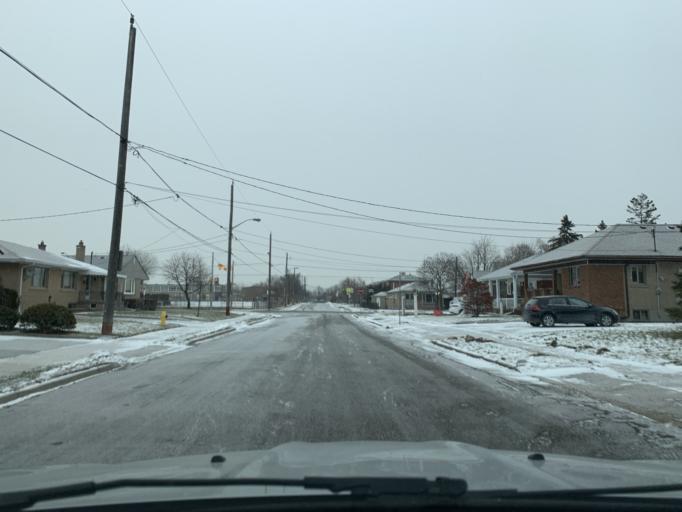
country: CA
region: Ontario
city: Toronto
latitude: 43.7319
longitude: -79.4697
